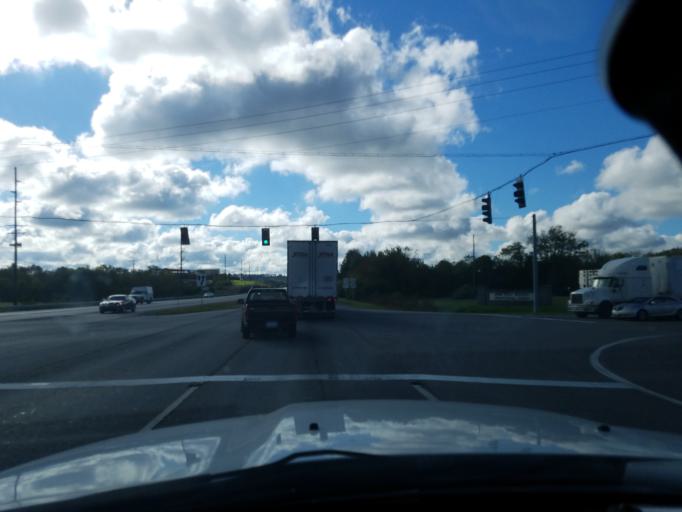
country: US
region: Kentucky
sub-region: Boyle County
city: Danville
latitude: 37.6292
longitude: -84.7979
